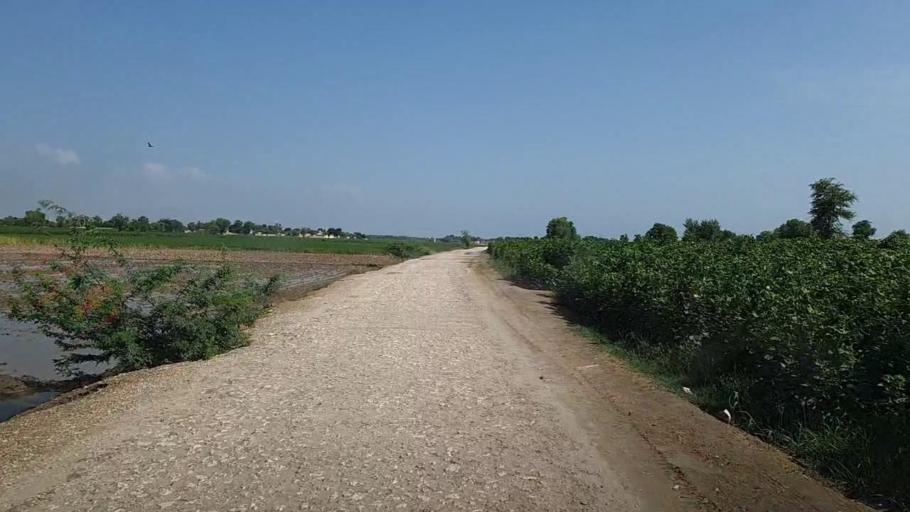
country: PK
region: Sindh
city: Bhiria
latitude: 26.8777
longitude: 68.2301
